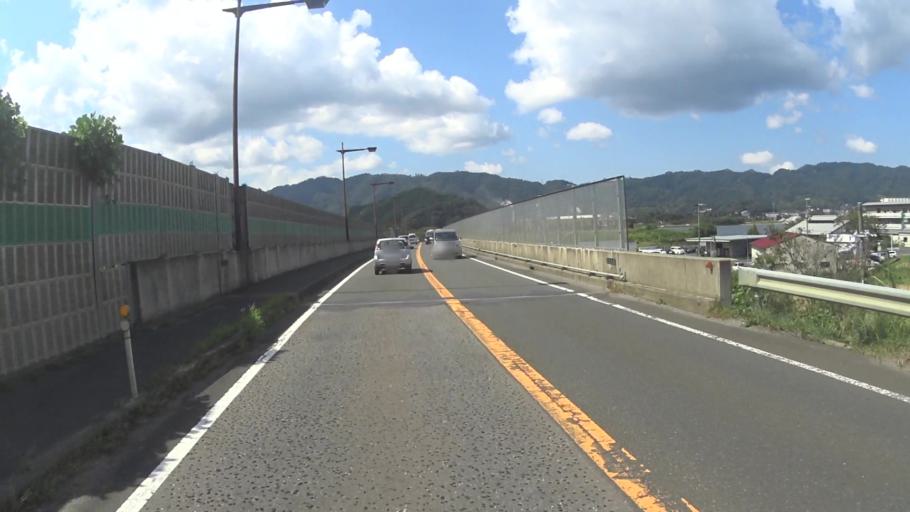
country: JP
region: Kyoto
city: Miyazu
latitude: 35.5517
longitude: 135.1604
